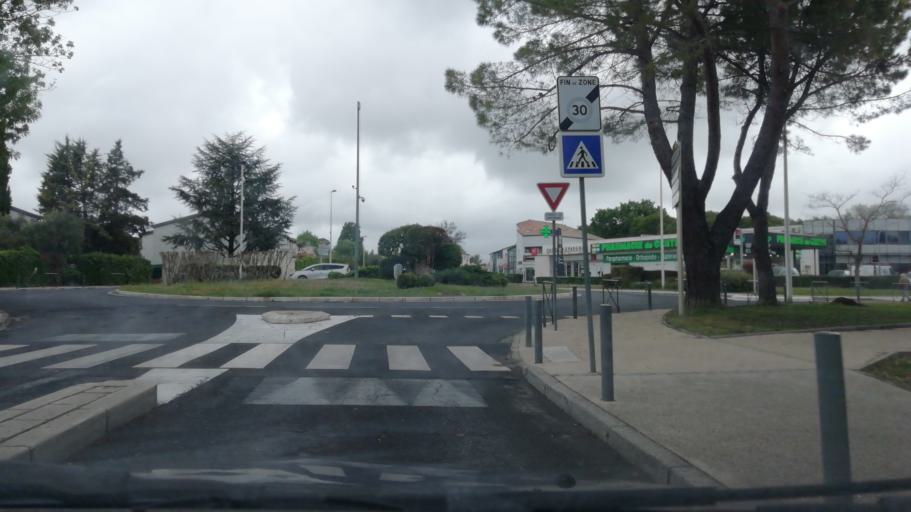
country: FR
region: Languedoc-Roussillon
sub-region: Departement de l'Herault
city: Saint-Gely-du-Fesc
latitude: 43.6942
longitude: 3.8068
